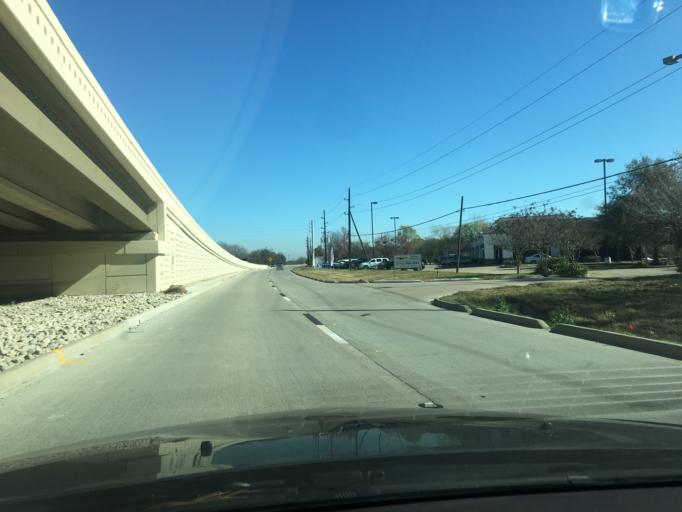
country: US
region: Texas
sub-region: Fort Bend County
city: Richmond
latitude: 29.5950
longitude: -95.7405
